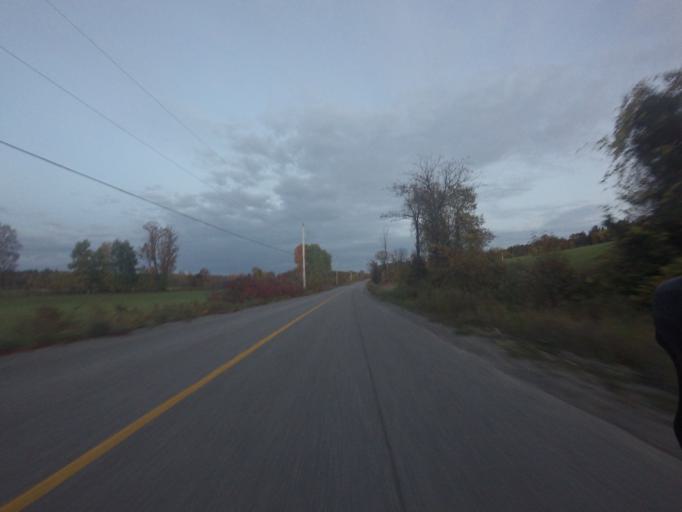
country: CA
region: Ontario
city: Renfrew
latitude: 45.3448
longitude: -76.9297
